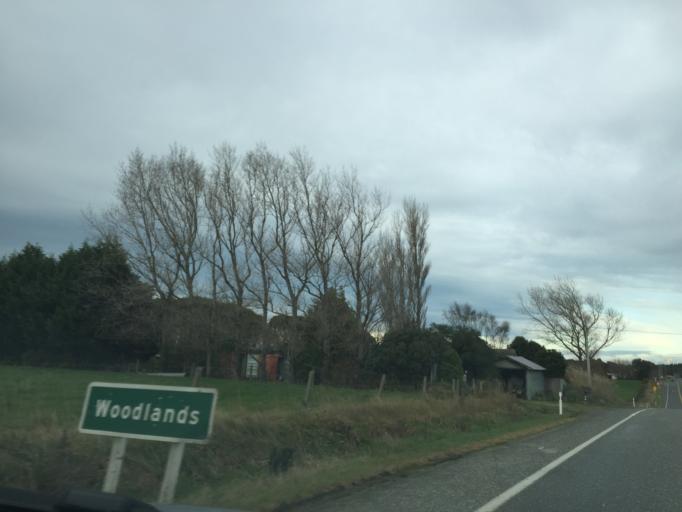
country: NZ
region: Southland
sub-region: Invercargill City
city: Invercargill
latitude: -46.3510
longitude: 168.5545
